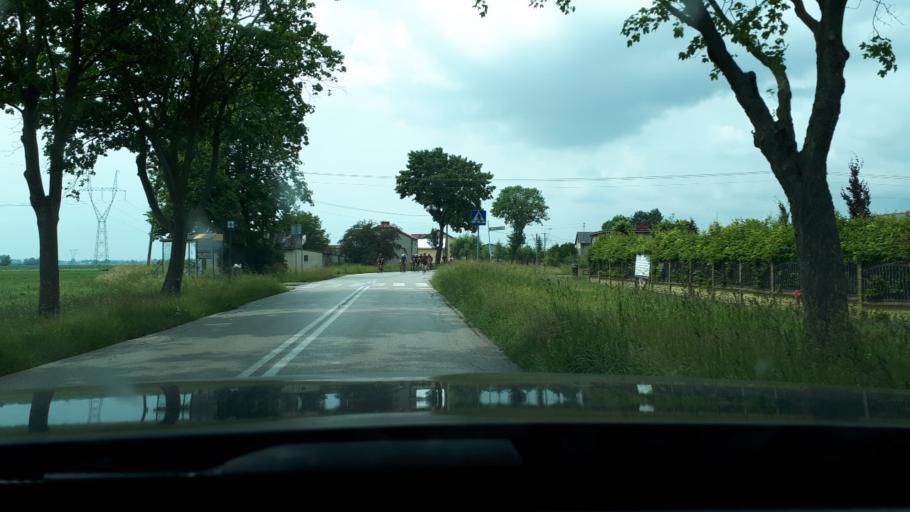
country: PL
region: Masovian Voivodeship
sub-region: Powiat warszawski zachodni
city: Jozefow
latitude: 52.2367
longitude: 20.6586
